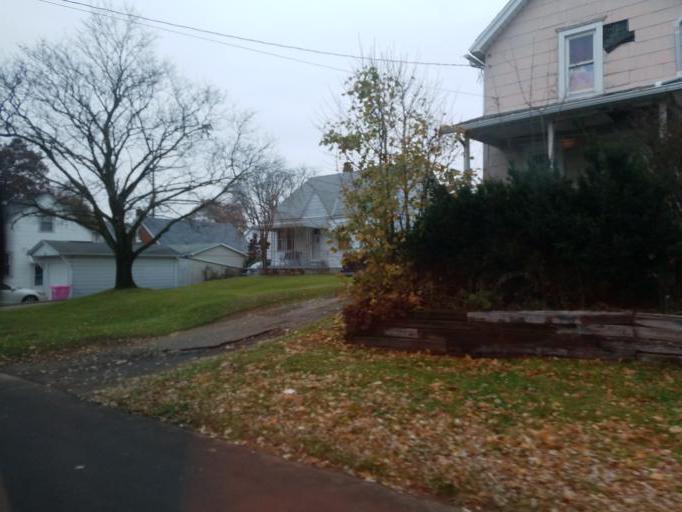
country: US
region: Ohio
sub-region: Richland County
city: Mansfield
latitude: 40.7413
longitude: -82.5224
